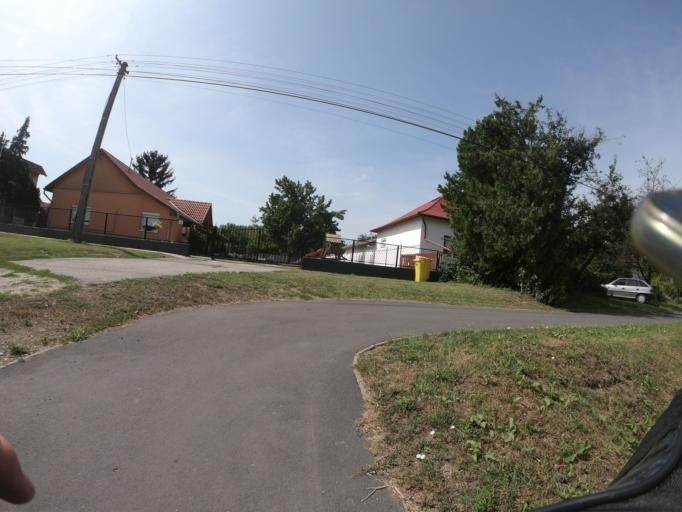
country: HU
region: Jasz-Nagykun-Szolnok
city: Tiszafured
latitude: 47.6072
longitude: 20.7658
